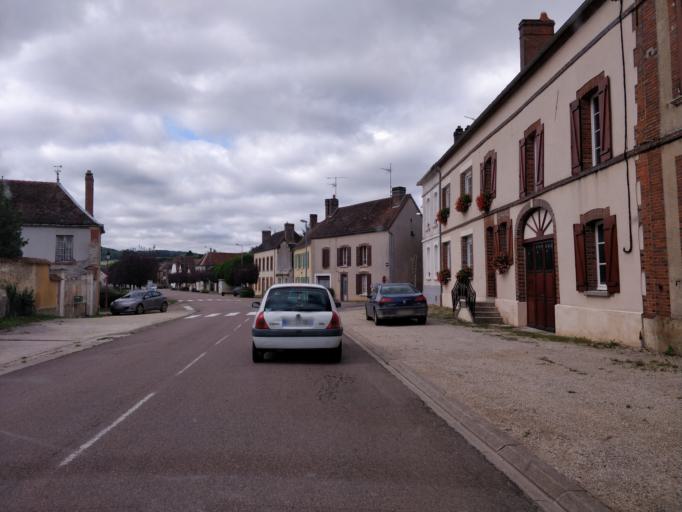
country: FR
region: Bourgogne
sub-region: Departement de l'Yonne
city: Saint-Florentin
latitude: 48.0829
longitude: 3.7030
